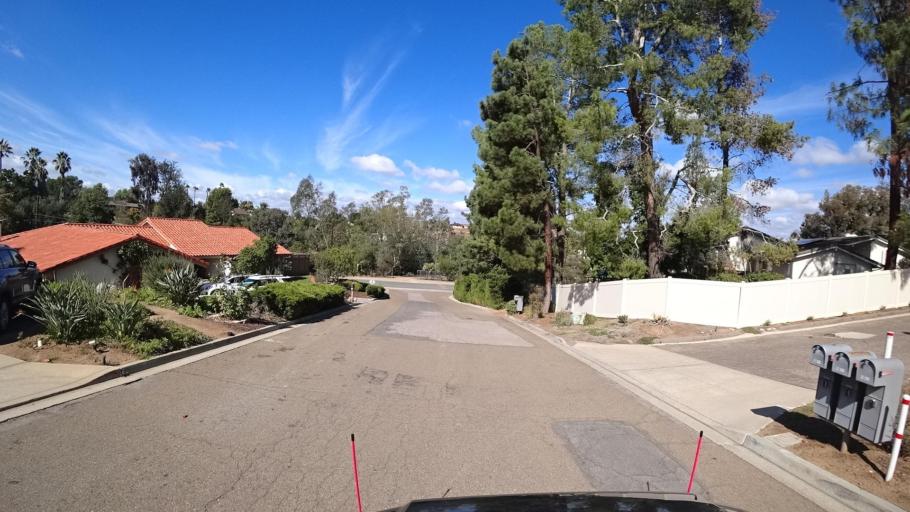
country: US
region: California
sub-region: San Diego County
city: Rancho San Diego
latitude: 32.7693
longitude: -116.9357
